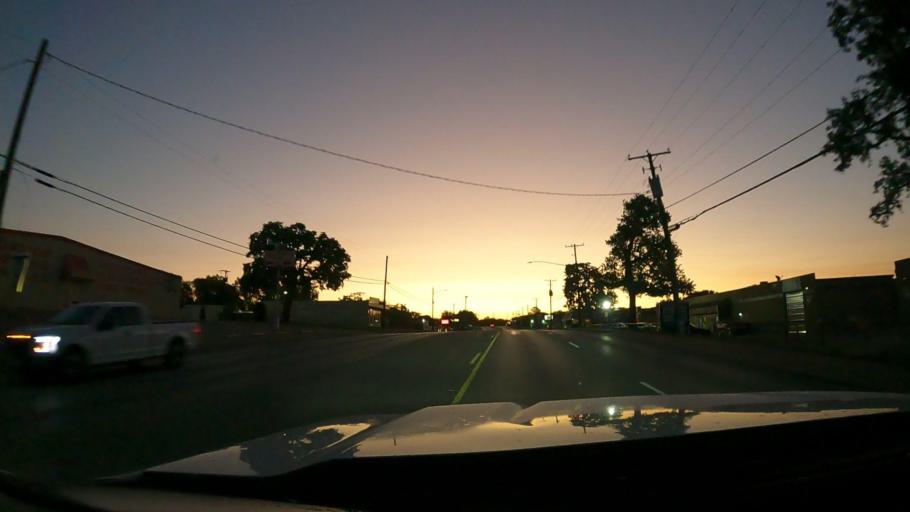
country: US
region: Texas
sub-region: Tarrant County
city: Pantego
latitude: 32.7358
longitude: -97.1377
